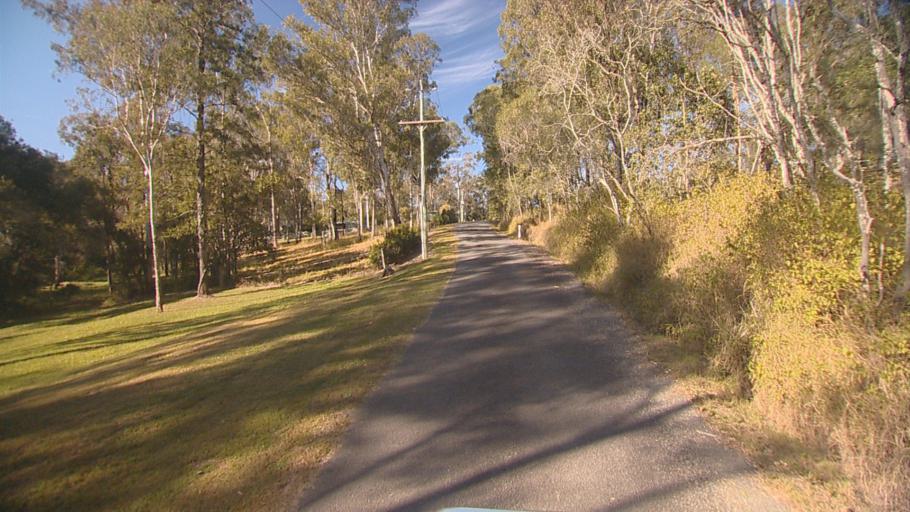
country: AU
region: Queensland
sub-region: Logan
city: Windaroo
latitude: -27.7948
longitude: 153.1738
